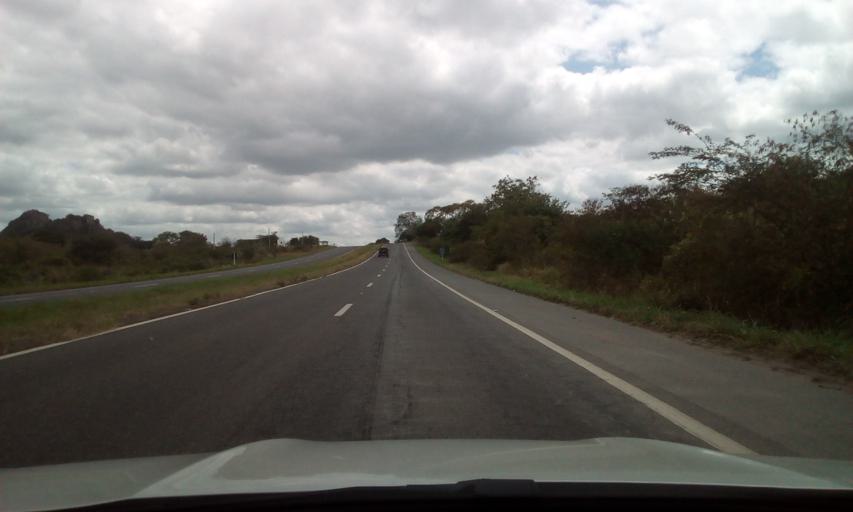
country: BR
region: Paraiba
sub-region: Fagundes
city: Fagundes
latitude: -7.2758
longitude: -35.7285
